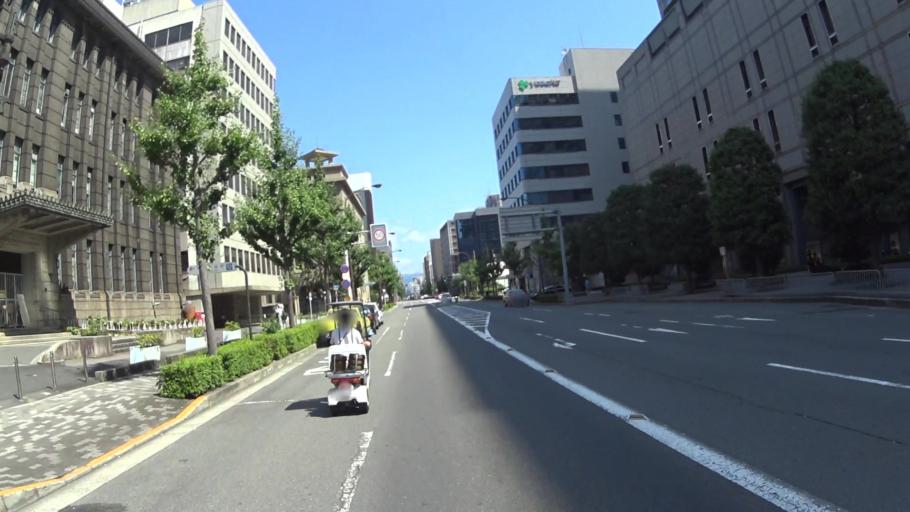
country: JP
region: Kyoto
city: Kyoto
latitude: 35.0109
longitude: 135.7693
